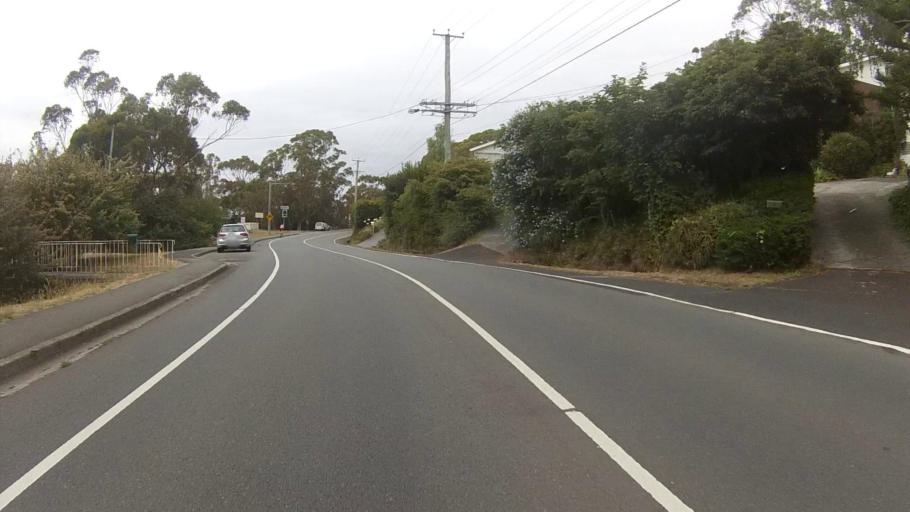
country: AU
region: Tasmania
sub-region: Kingborough
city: Taroona
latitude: -42.9410
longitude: 147.3525
